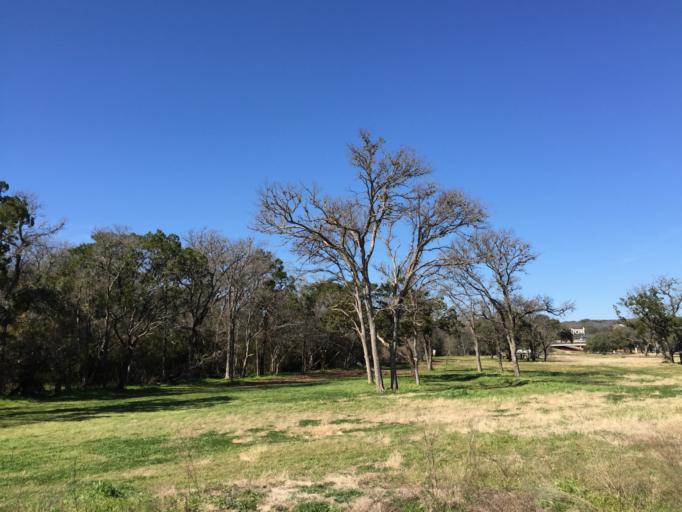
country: US
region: Texas
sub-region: Travis County
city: Rollingwood
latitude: 30.2664
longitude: -97.7754
